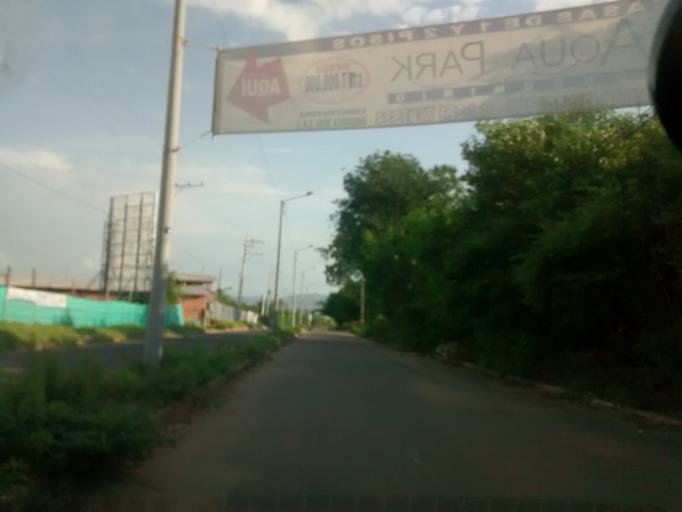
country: CO
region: Cundinamarca
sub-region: Girardot
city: Girardot City
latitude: 4.3147
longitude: -74.8175
